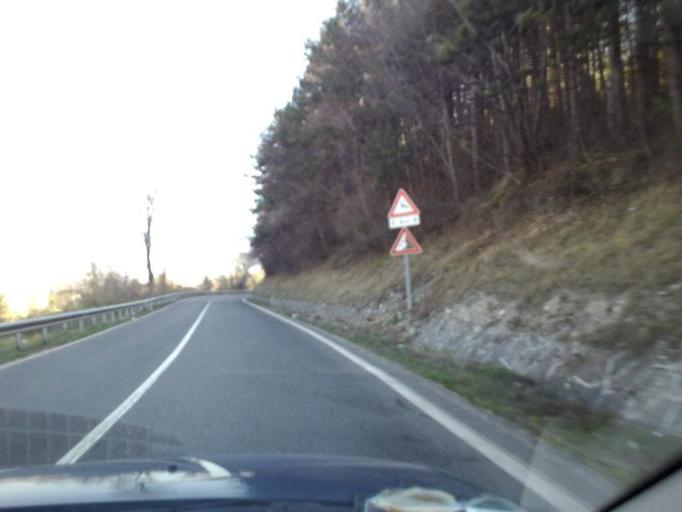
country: IT
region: Veneto
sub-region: Provincia di Verona
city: Cerro Veronese
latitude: 45.5573
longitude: 11.0397
